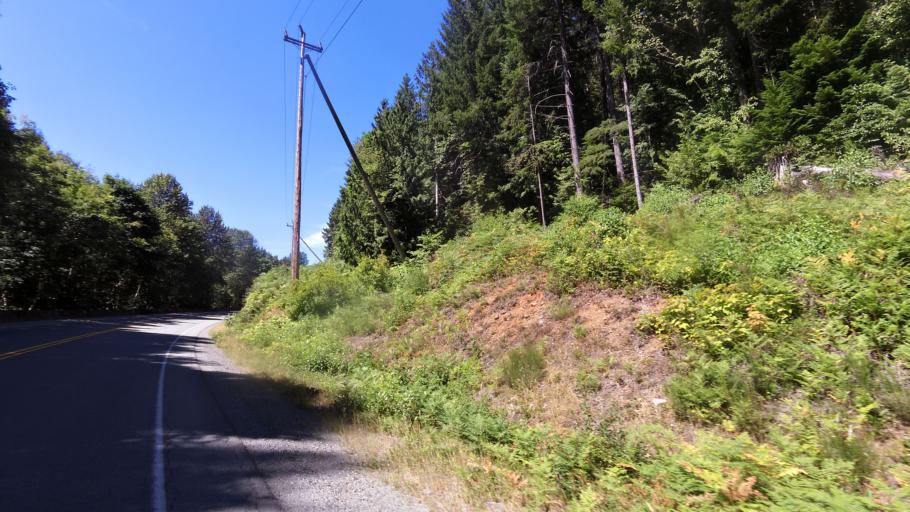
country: CA
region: British Columbia
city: Port Alberni
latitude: 49.2782
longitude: -125.1311
